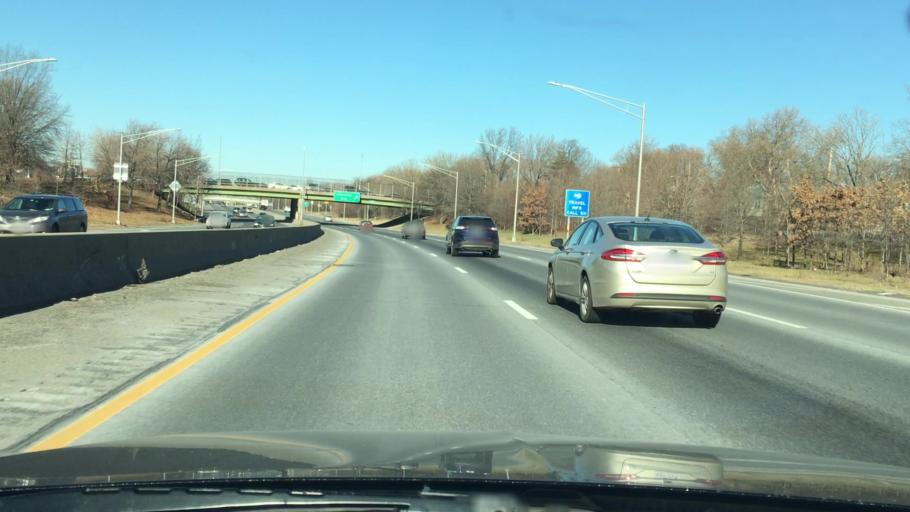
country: US
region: New York
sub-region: Bronx
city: The Bronx
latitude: 40.8268
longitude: -73.8169
